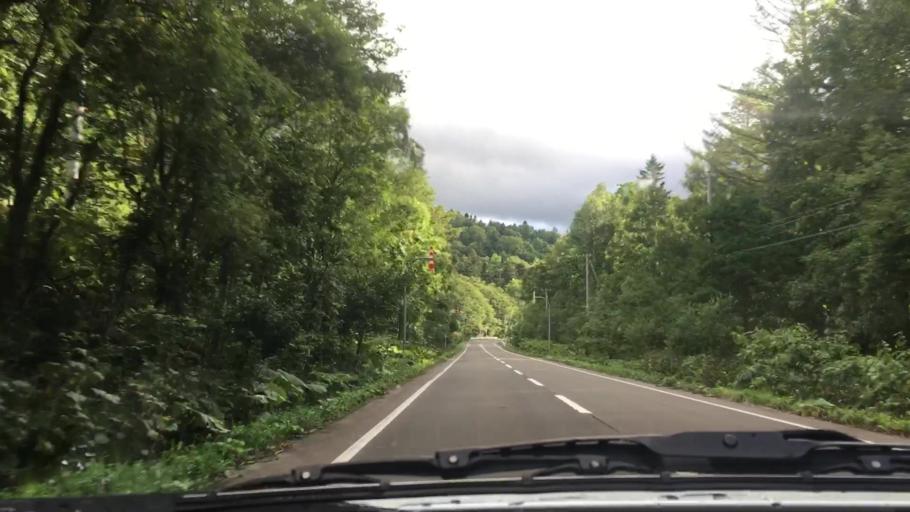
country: JP
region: Hokkaido
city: Shimo-furano
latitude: 43.0888
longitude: 142.6803
